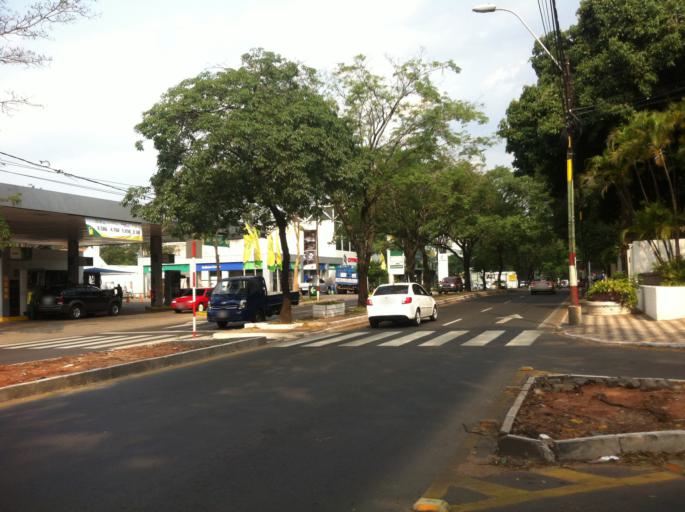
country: PY
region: Central
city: Fernando de la Mora
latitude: -25.2996
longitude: -57.5677
